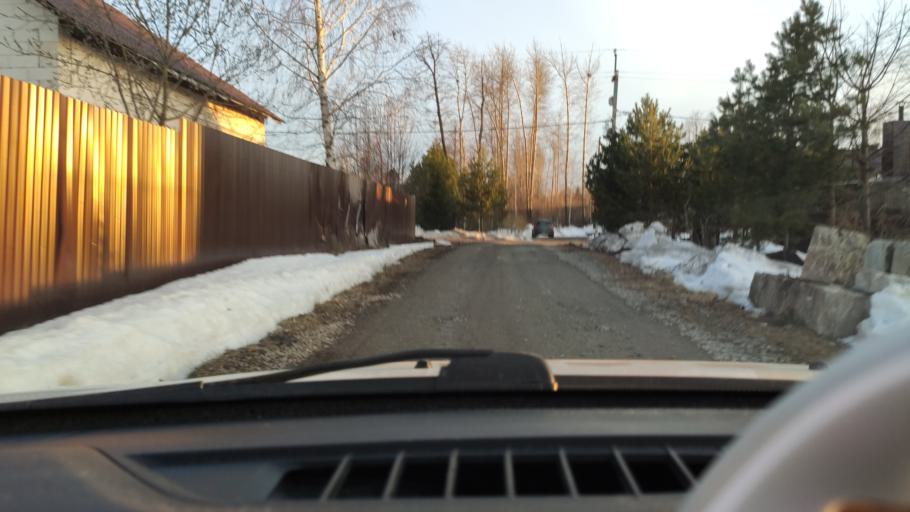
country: RU
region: Perm
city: Polazna
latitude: 58.1165
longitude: 56.4110
